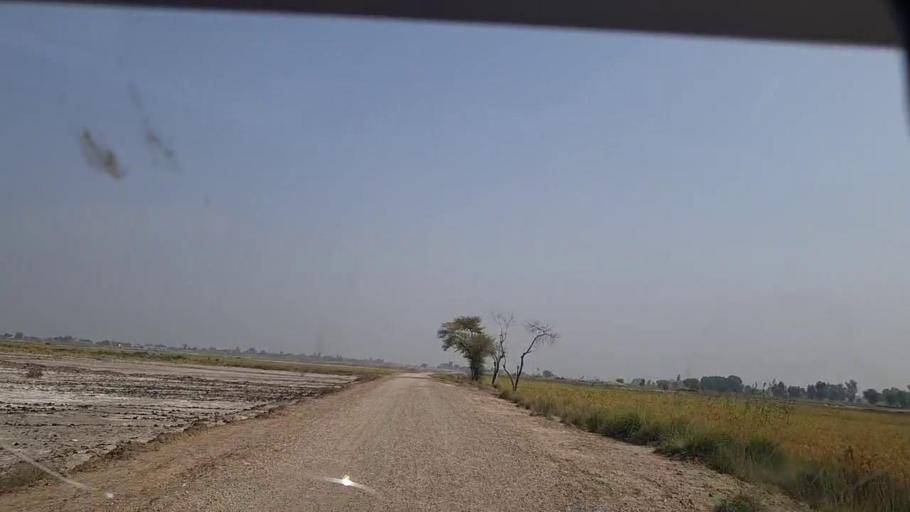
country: PK
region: Sindh
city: Shikarpur
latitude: 28.0512
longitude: 68.6603
